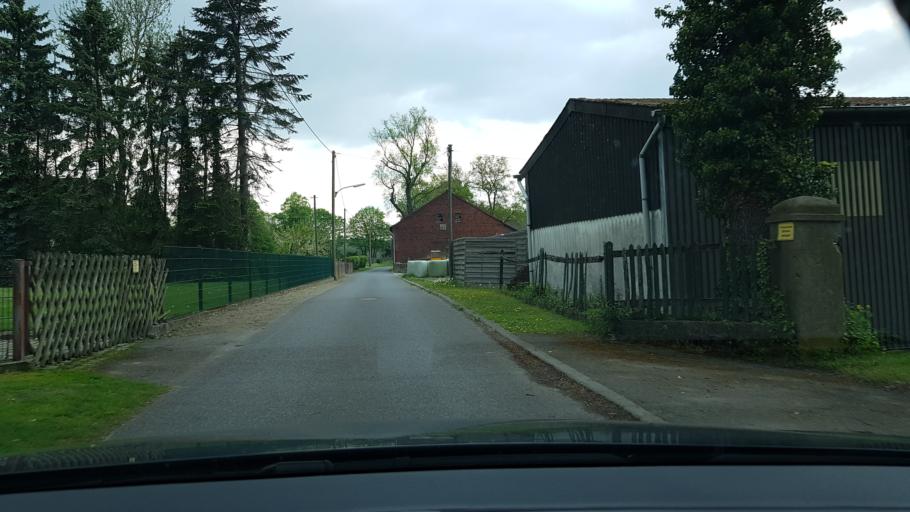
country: DE
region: North Rhine-Westphalia
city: Oer-Erkenschwick
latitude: 51.6402
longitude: 7.2330
